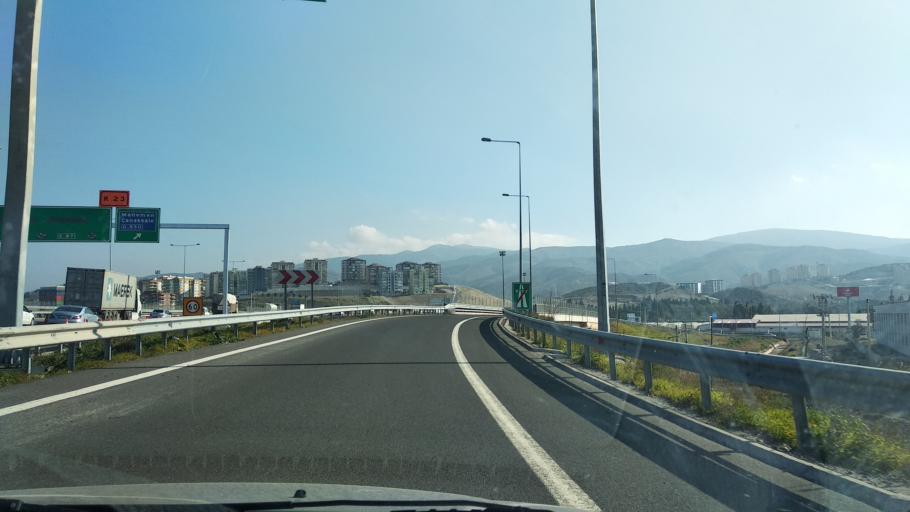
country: TR
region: Izmir
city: Menemen
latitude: 38.5707
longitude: 27.0517
